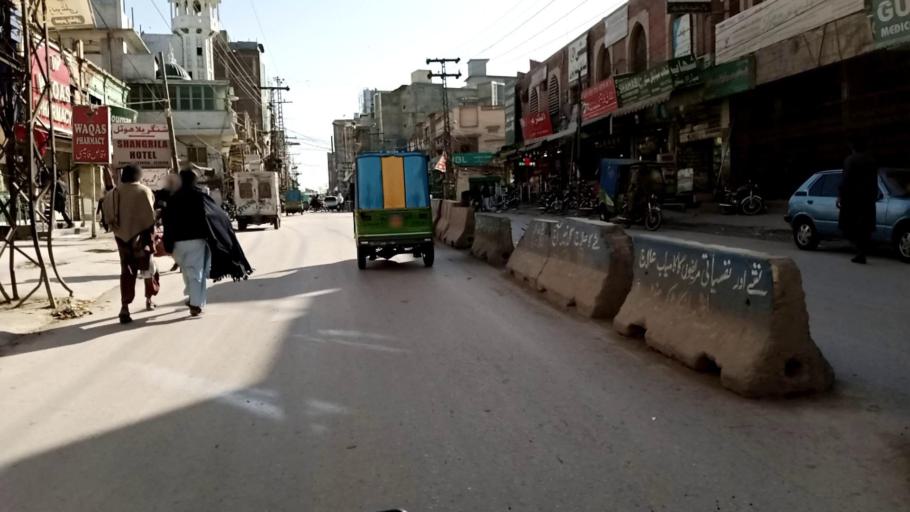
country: PK
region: Khyber Pakhtunkhwa
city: Peshawar
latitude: 34.0042
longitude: 71.5602
